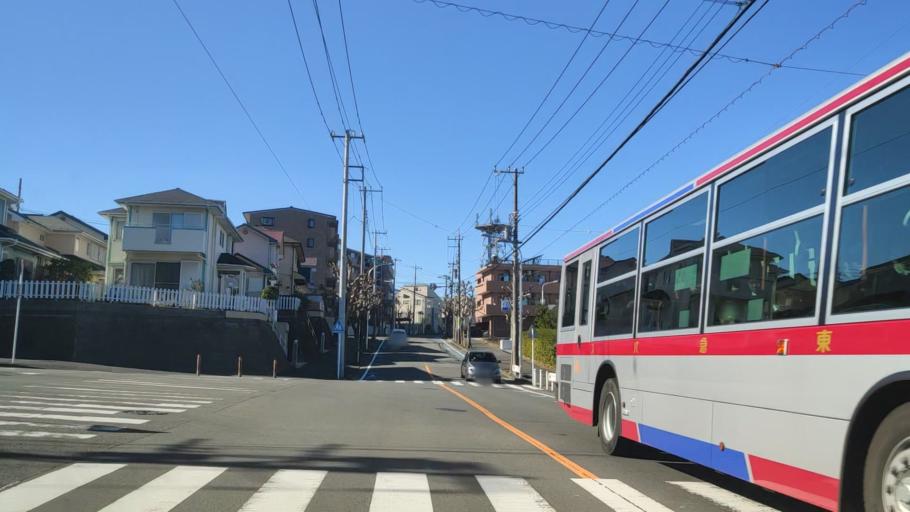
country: JP
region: Tokyo
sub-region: Machida-shi
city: Machida
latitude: 35.5547
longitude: 139.4977
